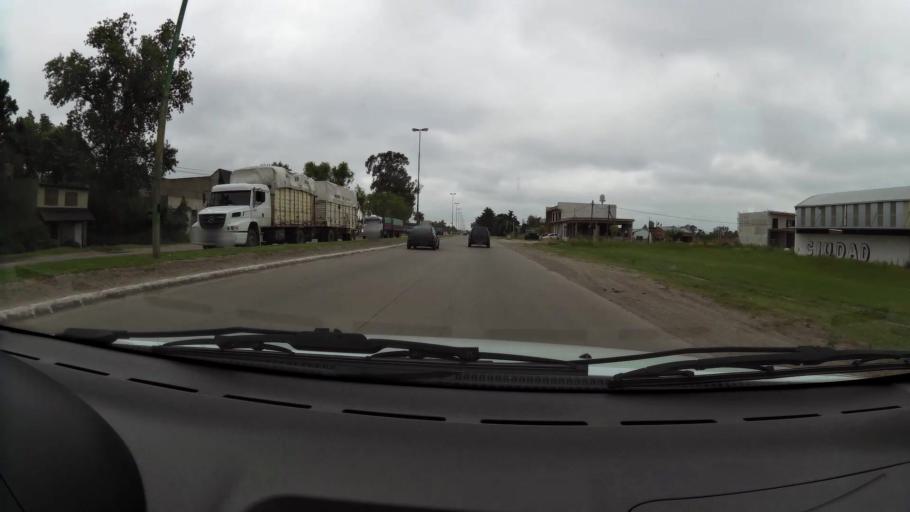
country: AR
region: Buenos Aires
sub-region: Partido de La Plata
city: La Plata
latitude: -35.0120
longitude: -58.0663
